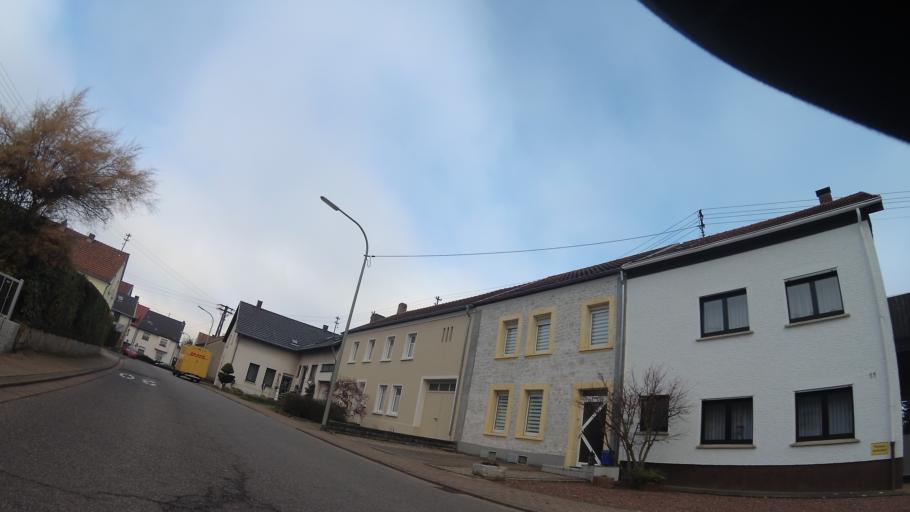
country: DE
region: Saarland
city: Schwalbach
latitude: 49.3038
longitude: 6.8189
